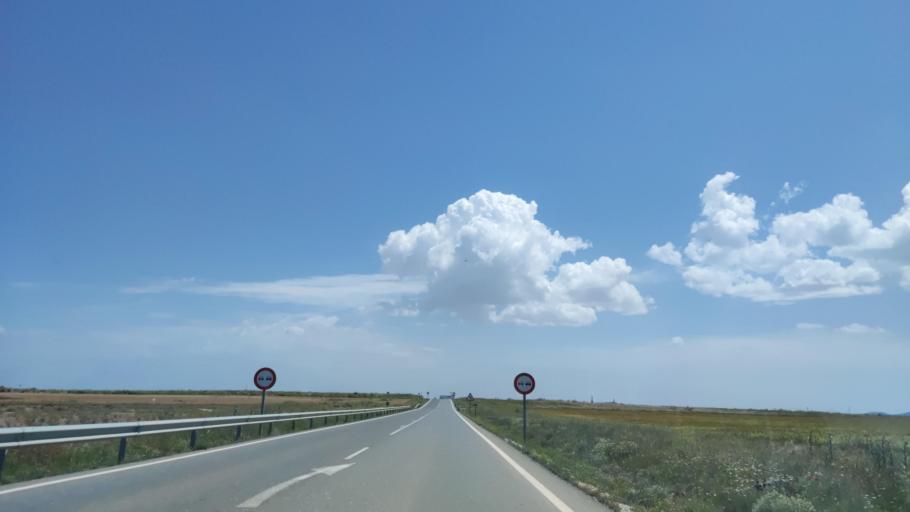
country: ES
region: Castille-La Mancha
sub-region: Province of Toledo
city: Mascaraque
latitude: 39.7154
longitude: -3.8248
